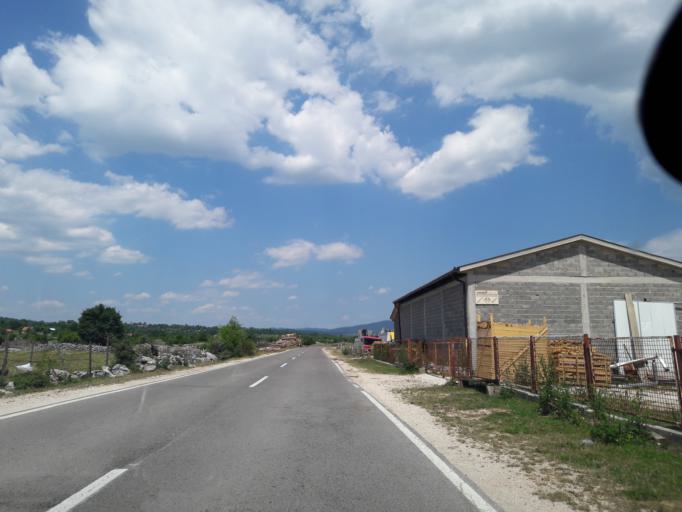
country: BA
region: Republika Srpska
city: Sipovo
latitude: 44.1571
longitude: 17.1695
